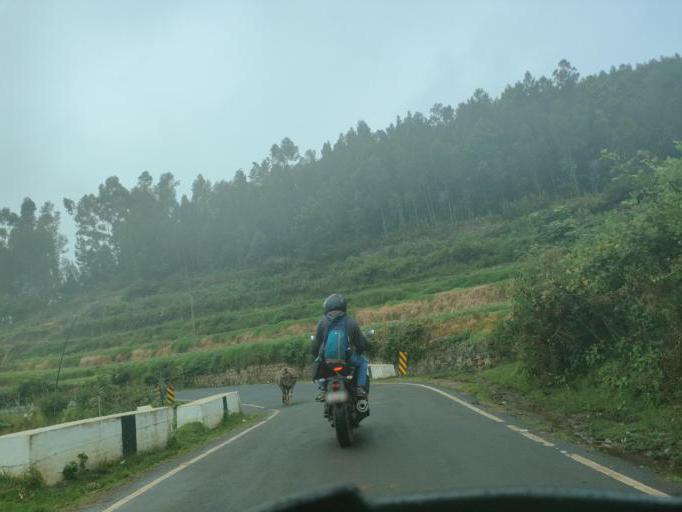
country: IN
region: Tamil Nadu
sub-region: Dindigul
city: Kodaikanal
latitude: 10.2267
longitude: 77.3504
